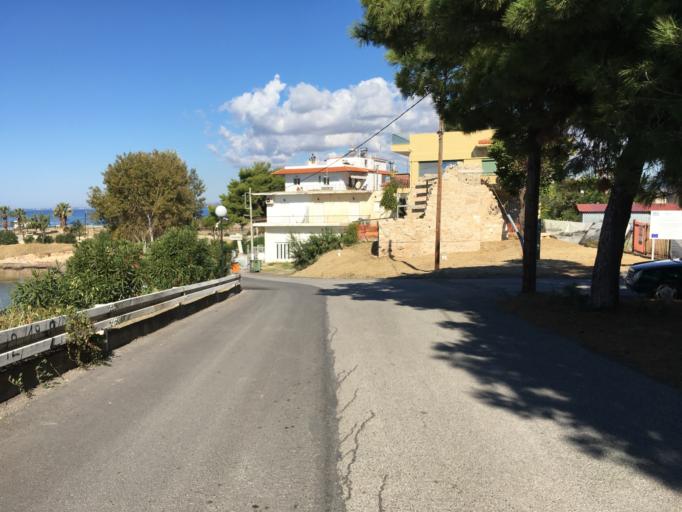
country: GR
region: Central Macedonia
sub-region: Nomos Chalkidikis
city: Nea Poteidaia
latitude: 40.1948
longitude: 23.3245
